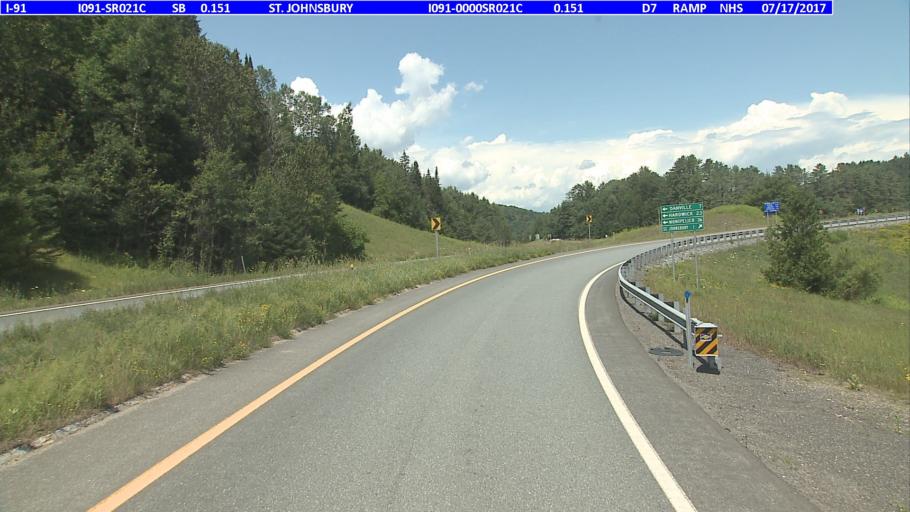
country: US
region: Vermont
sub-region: Caledonia County
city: St Johnsbury
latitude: 44.4274
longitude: -72.0364
